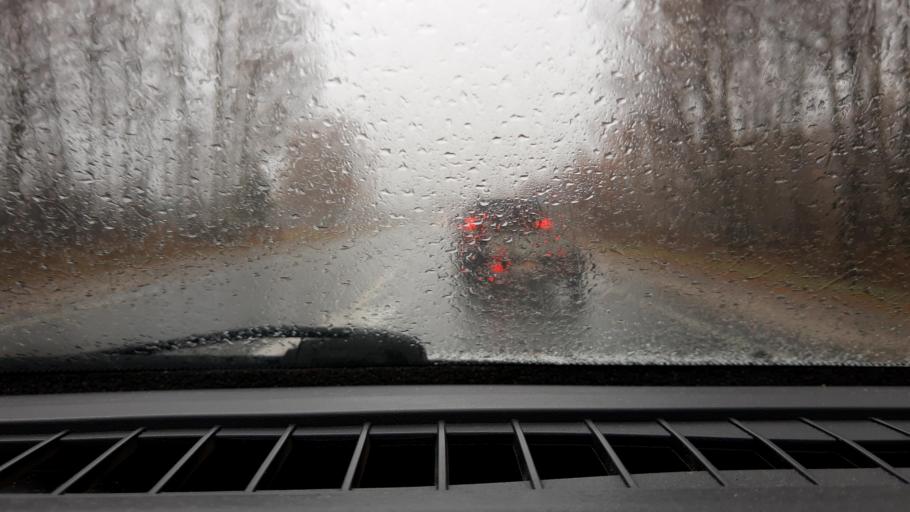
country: RU
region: Nizjnij Novgorod
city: Sitniki
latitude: 56.5297
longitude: 44.0245
